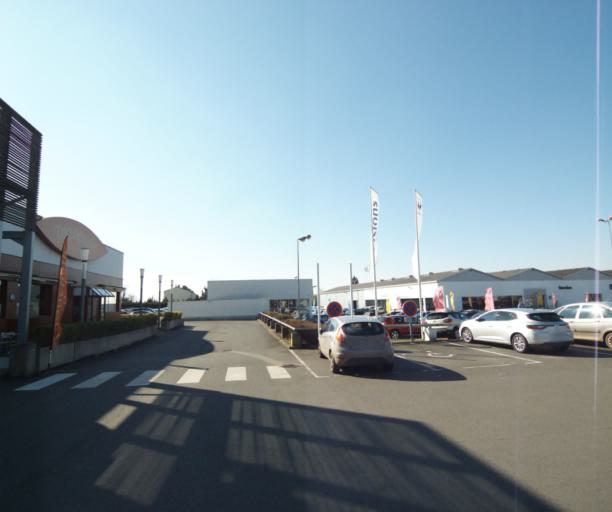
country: FR
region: Poitou-Charentes
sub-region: Departement des Deux-Sevres
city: Niort
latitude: 46.3292
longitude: -0.4418
